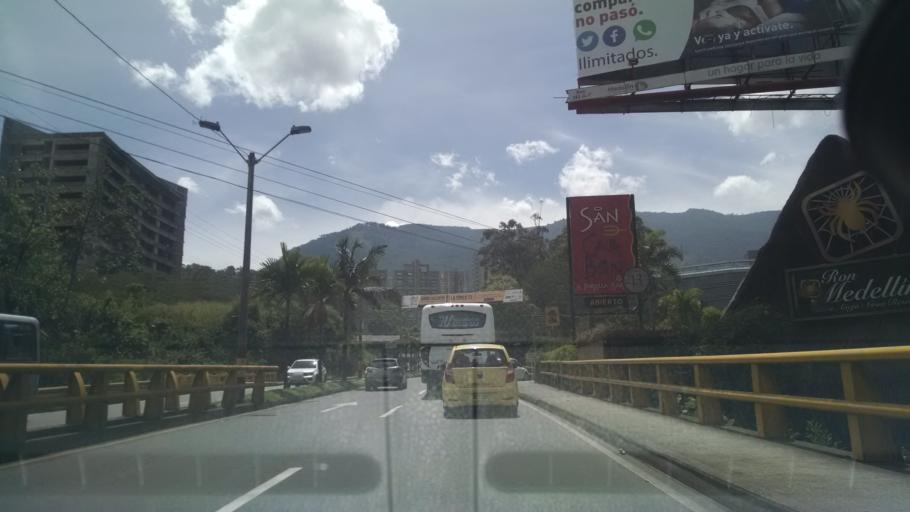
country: CO
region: Antioquia
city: Medellin
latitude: 6.2151
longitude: -75.5613
